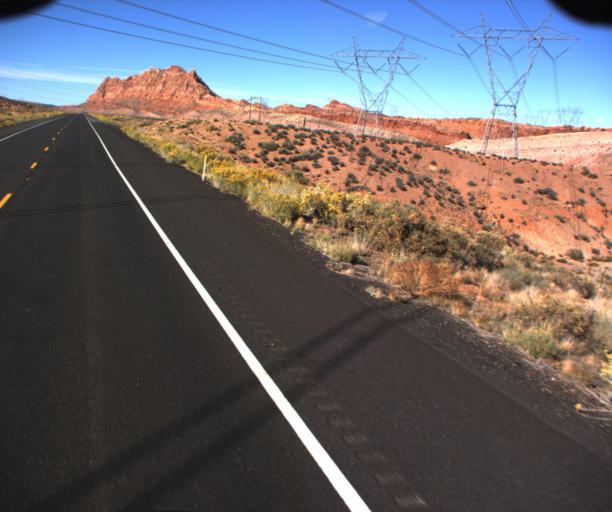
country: US
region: Arizona
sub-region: Coconino County
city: Tuba City
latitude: 36.2879
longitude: -111.4473
